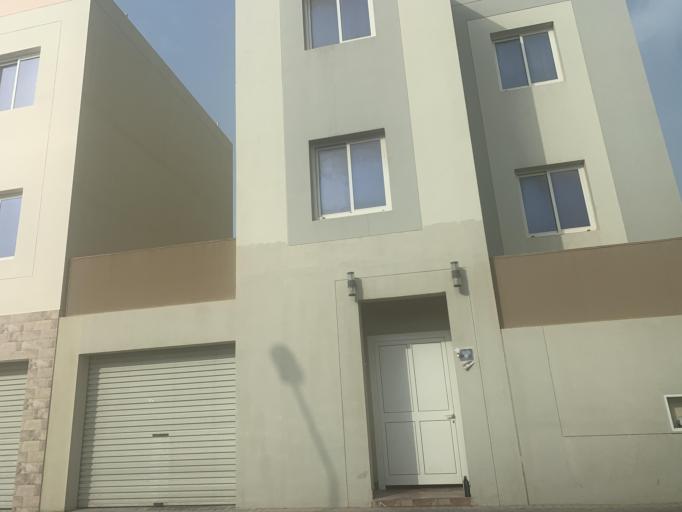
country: BH
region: Manama
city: Jidd Hafs
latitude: 26.2264
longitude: 50.4535
